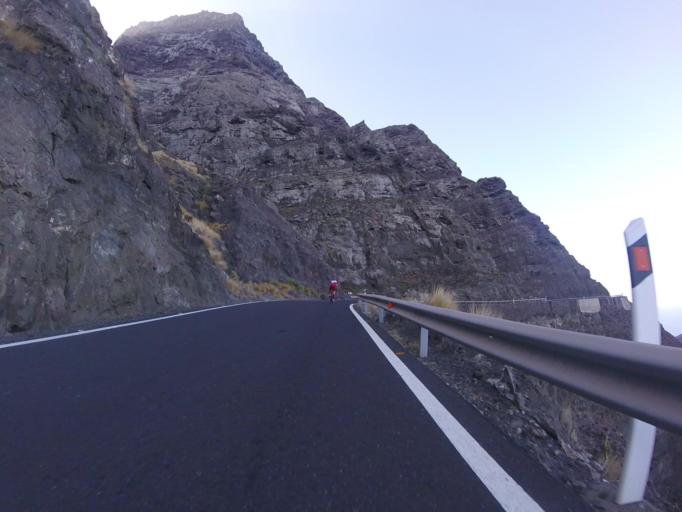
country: ES
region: Canary Islands
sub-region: Provincia de Las Palmas
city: Agaete
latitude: 28.0674
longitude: -15.7223
